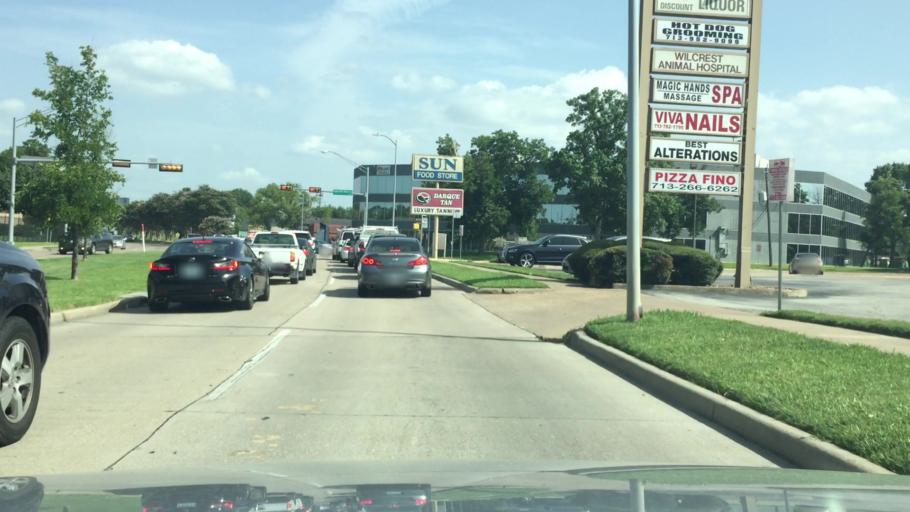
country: US
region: Texas
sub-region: Harris County
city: Bunker Hill Village
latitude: 29.7564
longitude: -95.5761
